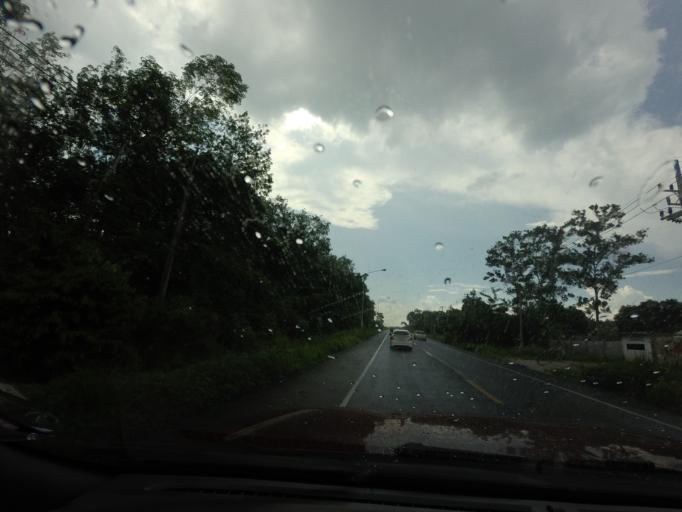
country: TH
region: Pattani
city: Mae Lan
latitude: 6.6558
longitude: 101.1727
